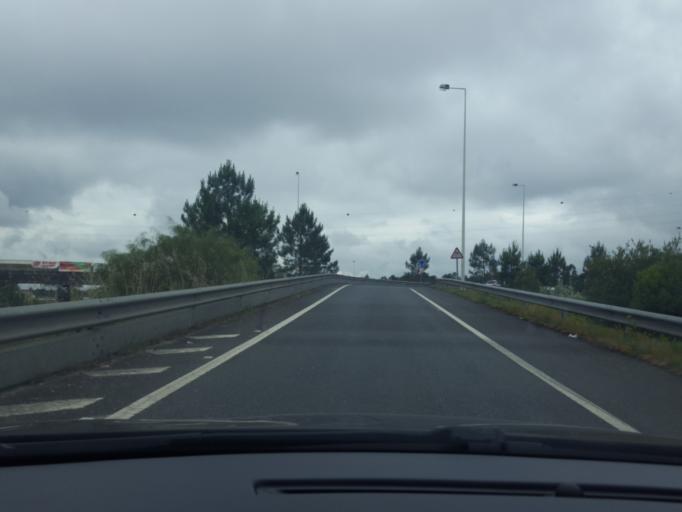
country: PT
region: Leiria
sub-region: Leiria
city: Leiria
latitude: 39.7668
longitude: -8.7769
